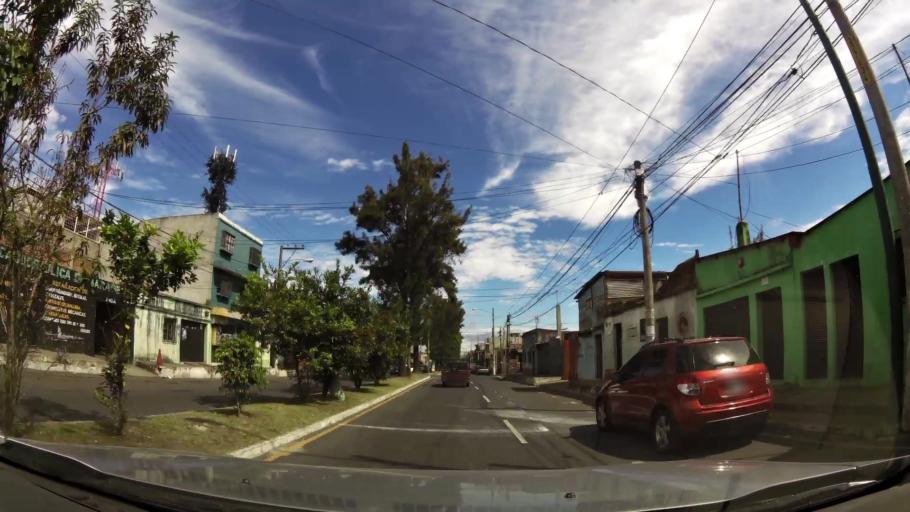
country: GT
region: Guatemala
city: Mixco
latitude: 14.6562
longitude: -90.5829
